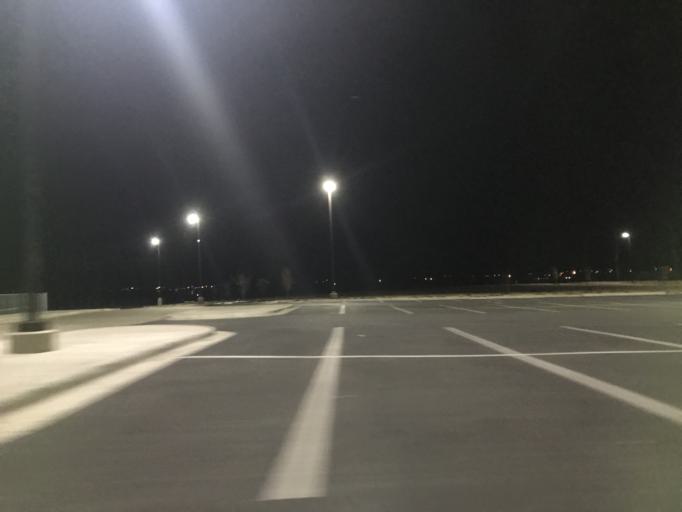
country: US
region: Texas
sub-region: Taylor County
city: Potosi
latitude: 32.3734
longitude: -99.7157
